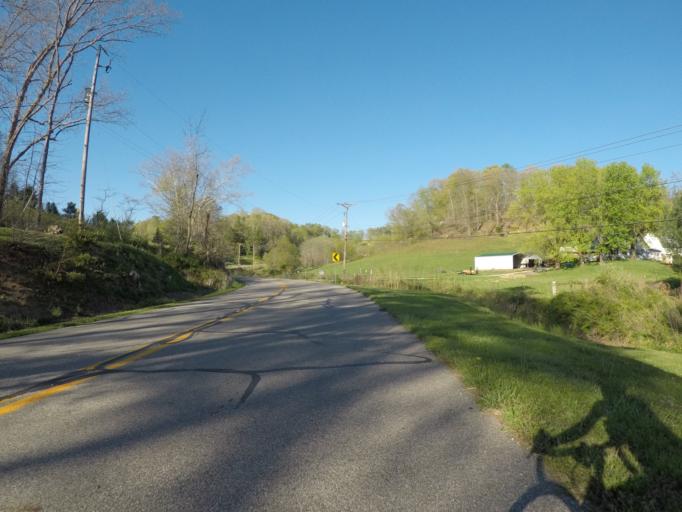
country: US
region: Kentucky
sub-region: Boyd County
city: Meads
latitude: 38.3689
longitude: -82.6621
